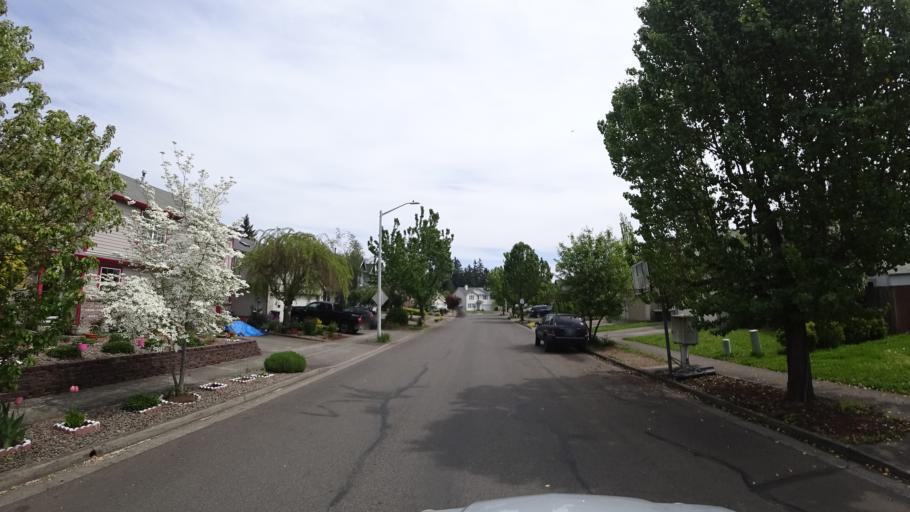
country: US
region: Oregon
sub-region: Washington County
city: Hillsboro
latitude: 45.5080
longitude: -122.9510
